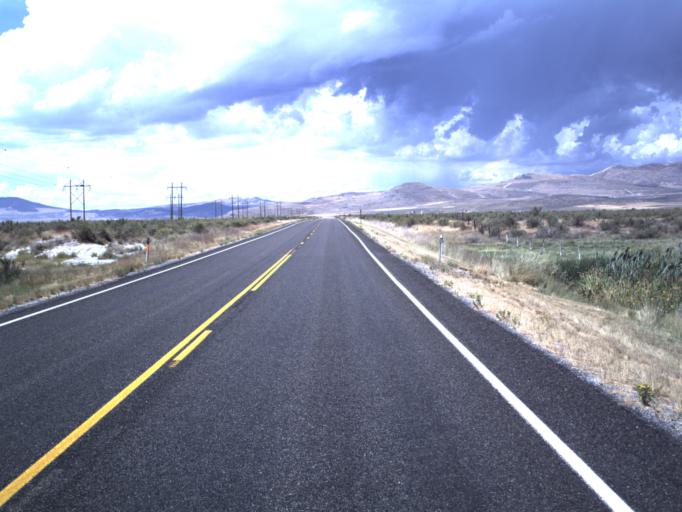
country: US
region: Utah
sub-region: Box Elder County
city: Tremonton
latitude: 41.5971
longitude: -112.2929
